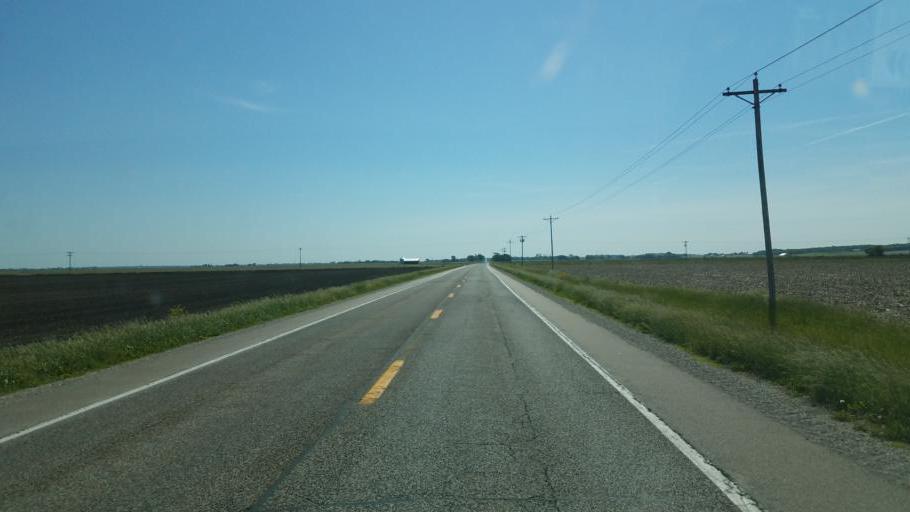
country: US
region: Illinois
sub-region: Mason County
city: Mason City
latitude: 40.3046
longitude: -89.7179
